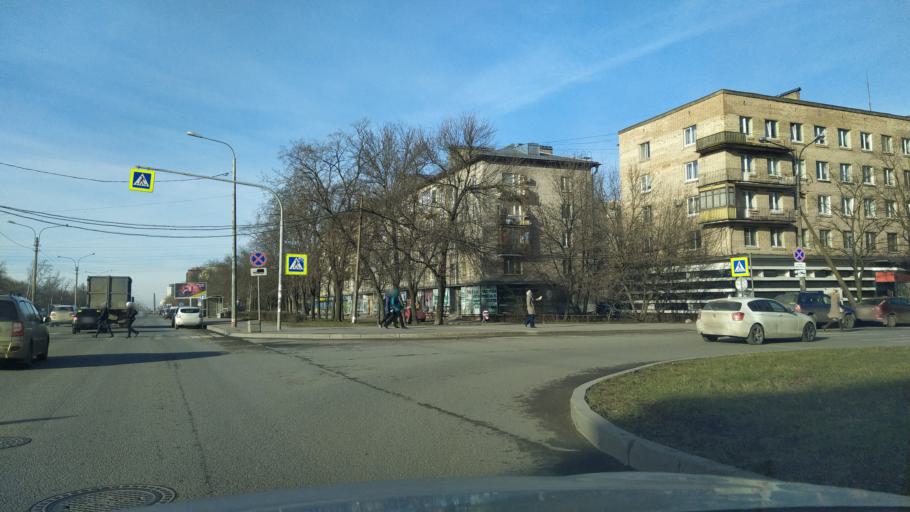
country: RU
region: St.-Petersburg
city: Kupchino
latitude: 59.8313
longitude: 30.3438
